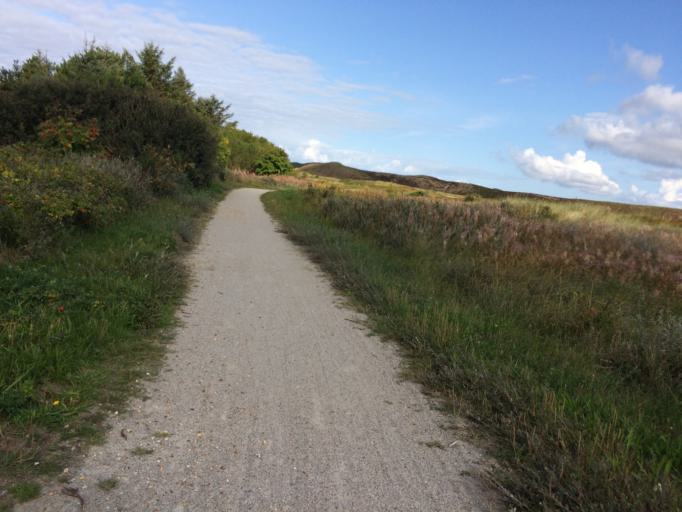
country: DK
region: Central Jutland
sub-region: Ringkobing-Skjern Kommune
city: Hvide Sande
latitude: 55.8927
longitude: 8.1691
